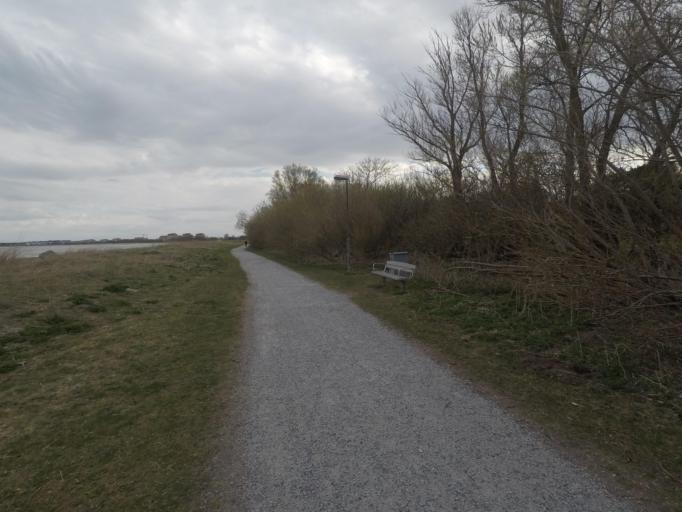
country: SE
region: Skane
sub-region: Lomma Kommun
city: Lomma
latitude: 55.6605
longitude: 13.0581
